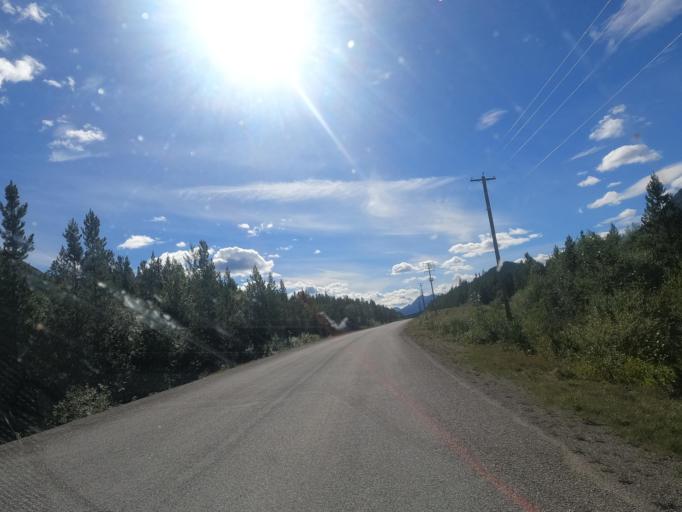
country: CA
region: Yukon
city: Watson Lake
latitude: 59.2766
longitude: -129.5534
